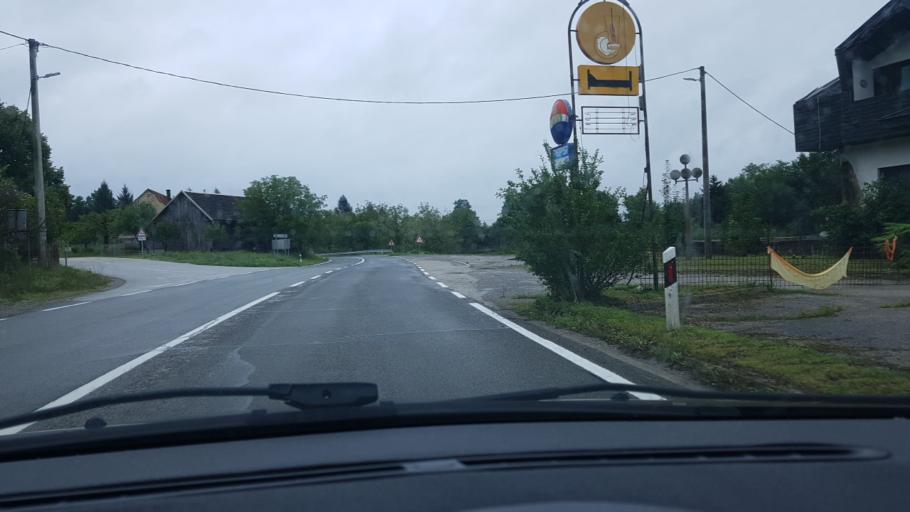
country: SI
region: Crnomelj
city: Crnomelj
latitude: 45.4481
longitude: 15.3335
